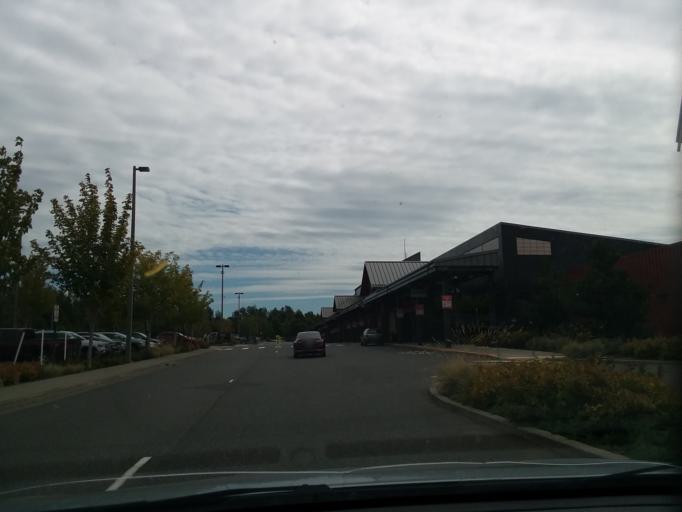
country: US
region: Washington
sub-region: Whatcom County
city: Marietta-Alderwood
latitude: 48.7965
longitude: -122.5337
